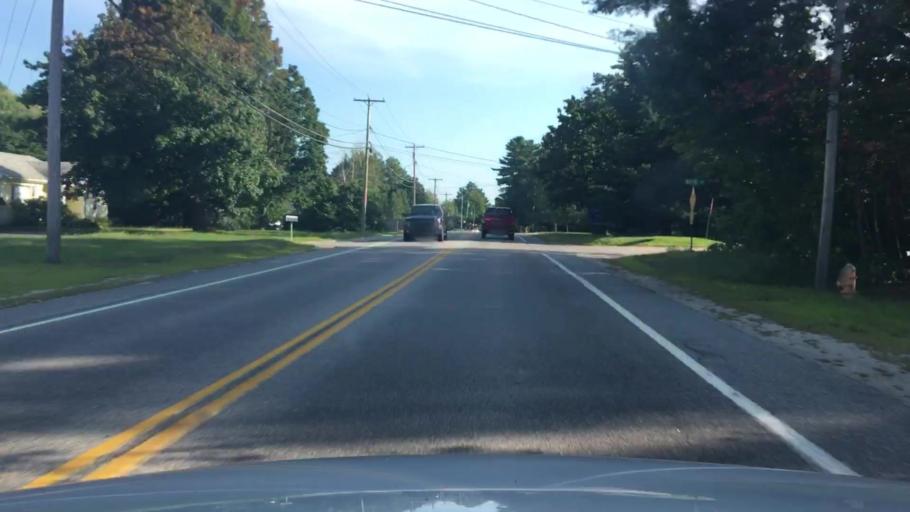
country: US
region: Maine
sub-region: Cumberland County
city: New Gloucester
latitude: 43.8943
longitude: -70.3282
